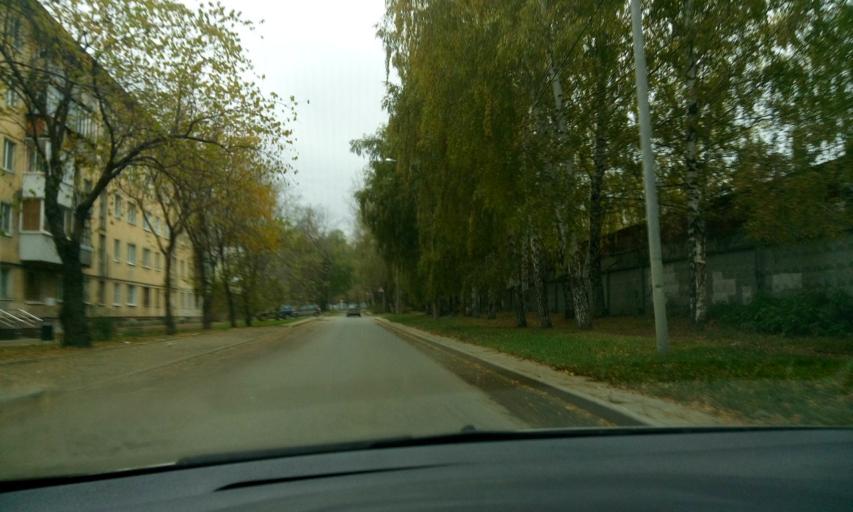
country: RU
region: Sverdlovsk
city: Yekaterinburg
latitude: 56.8505
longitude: 60.6457
